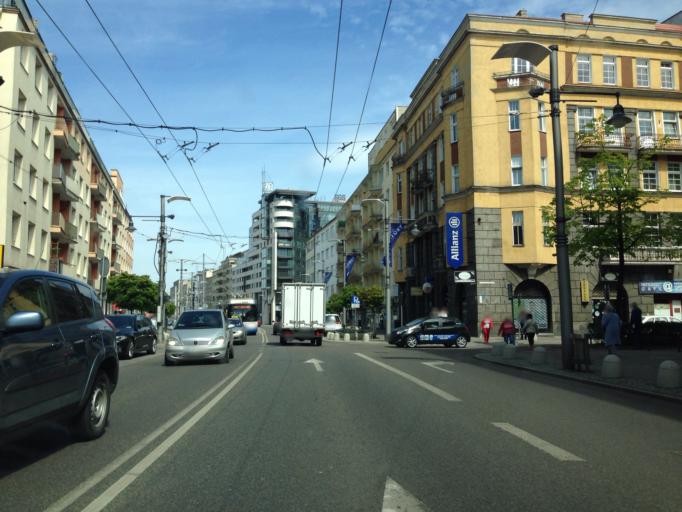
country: PL
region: Pomeranian Voivodeship
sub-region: Gdynia
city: Gdynia
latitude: 54.5204
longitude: 18.5430
